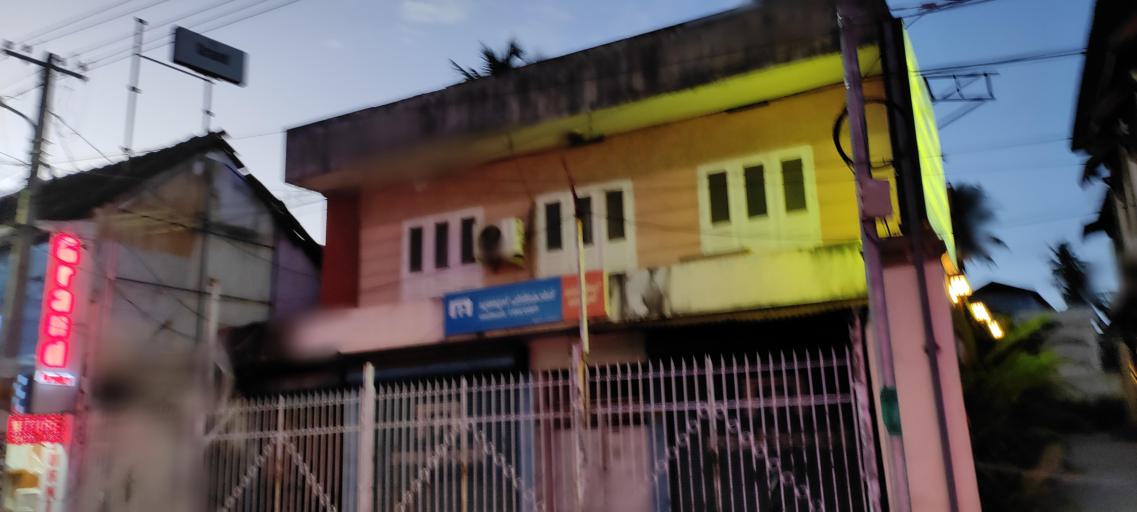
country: IN
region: Kerala
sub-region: Thiruvananthapuram
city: Thiruvananthapuram
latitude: 8.4818
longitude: 76.9558
